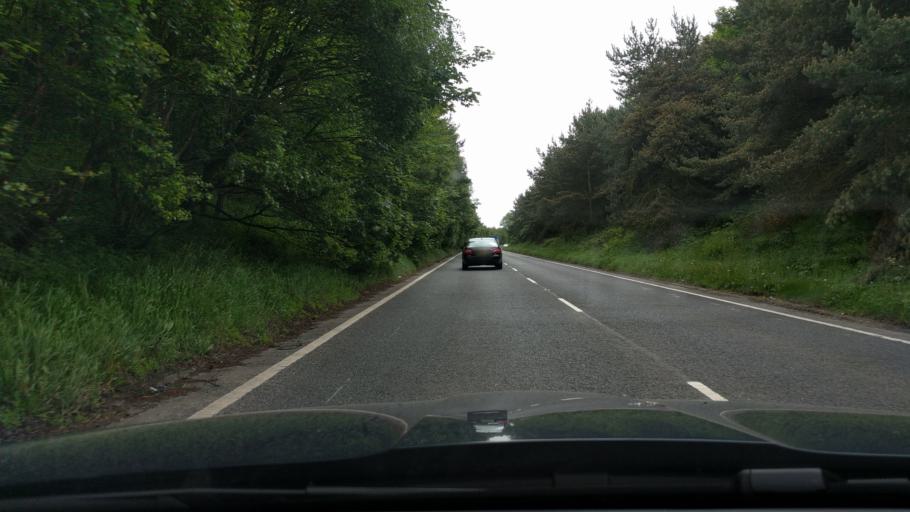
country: GB
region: England
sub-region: Northumberland
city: Lynemouth
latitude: 55.1945
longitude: -1.5445
